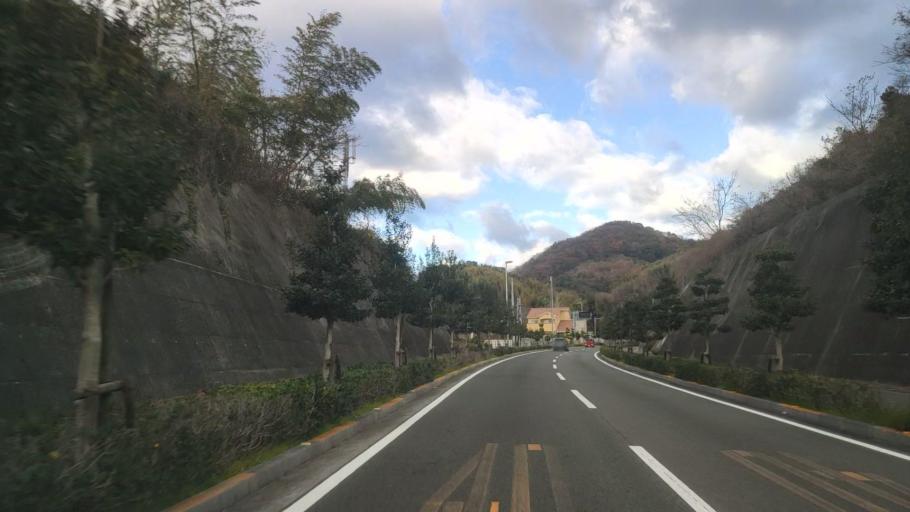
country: JP
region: Ehime
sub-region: Shikoku-chuo Shi
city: Matsuyama
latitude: 33.8743
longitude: 132.7161
